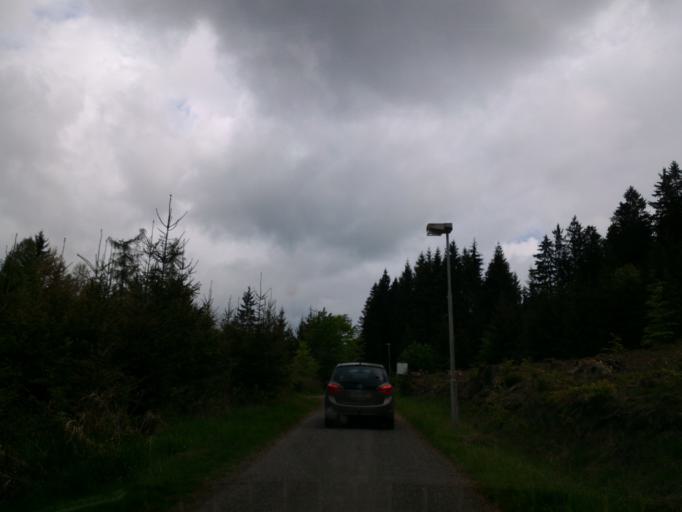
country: CZ
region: Vysocina
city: Ledec nad Sazavou
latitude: 49.6350
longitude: 15.3021
